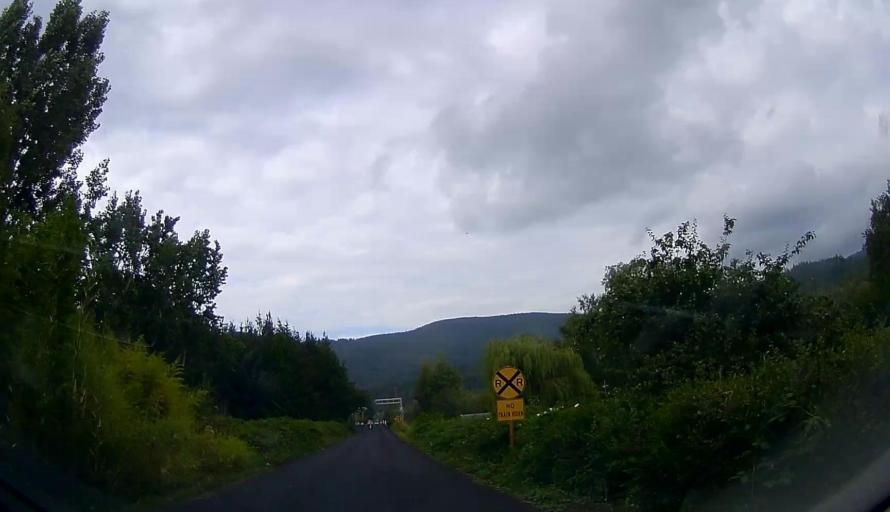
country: US
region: Washington
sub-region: Skagit County
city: Burlington
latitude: 48.5891
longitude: -122.4165
